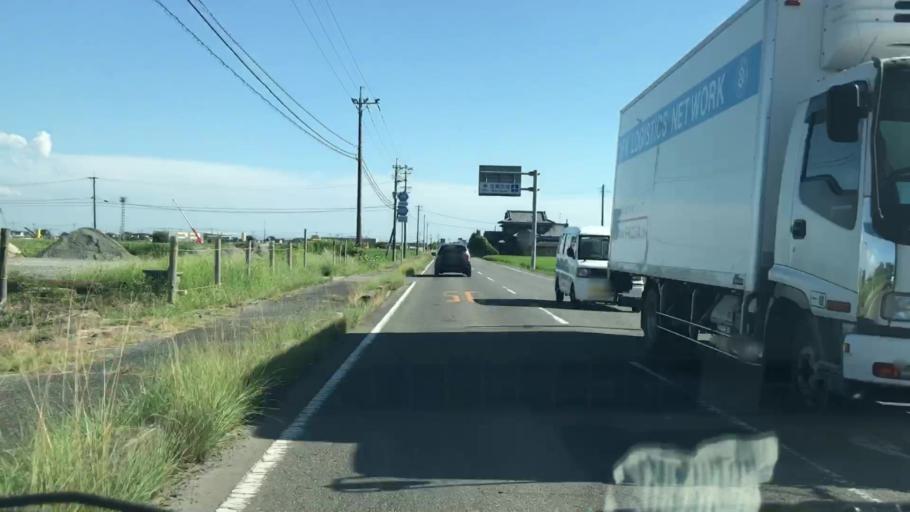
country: JP
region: Saga Prefecture
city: Okawa
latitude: 33.2187
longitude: 130.3345
